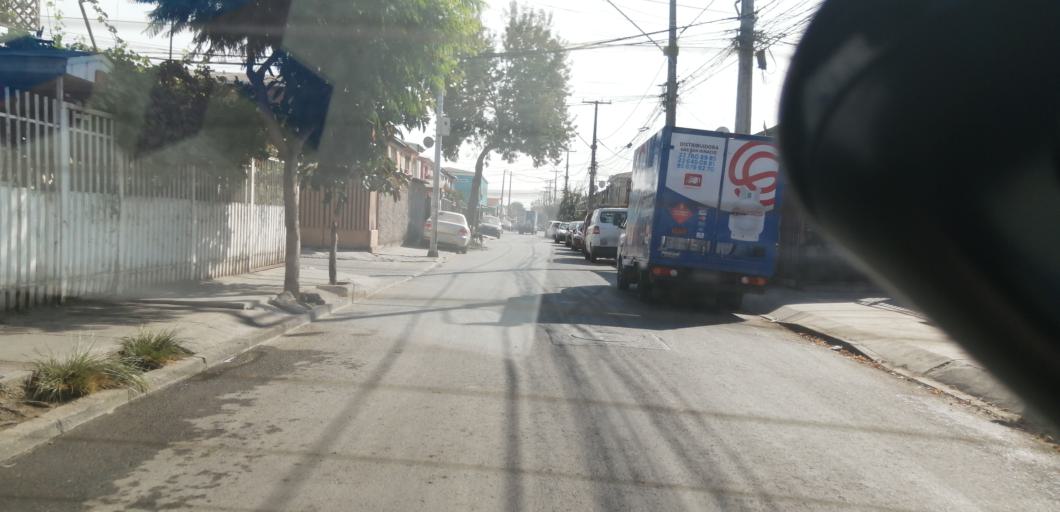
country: CL
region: Santiago Metropolitan
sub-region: Provincia de Santiago
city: Lo Prado
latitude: -33.4654
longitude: -70.7503
